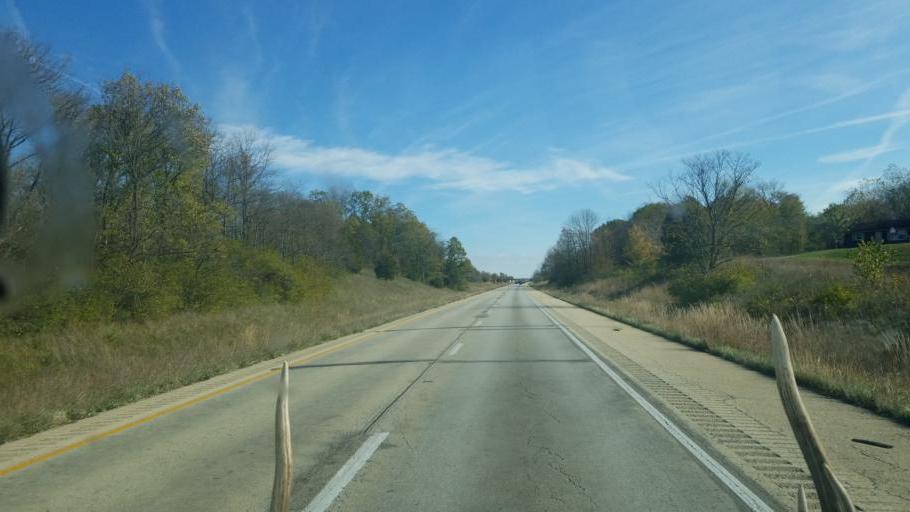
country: US
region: Illinois
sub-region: Effingham County
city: Effingham
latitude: 39.0804
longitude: -88.6290
